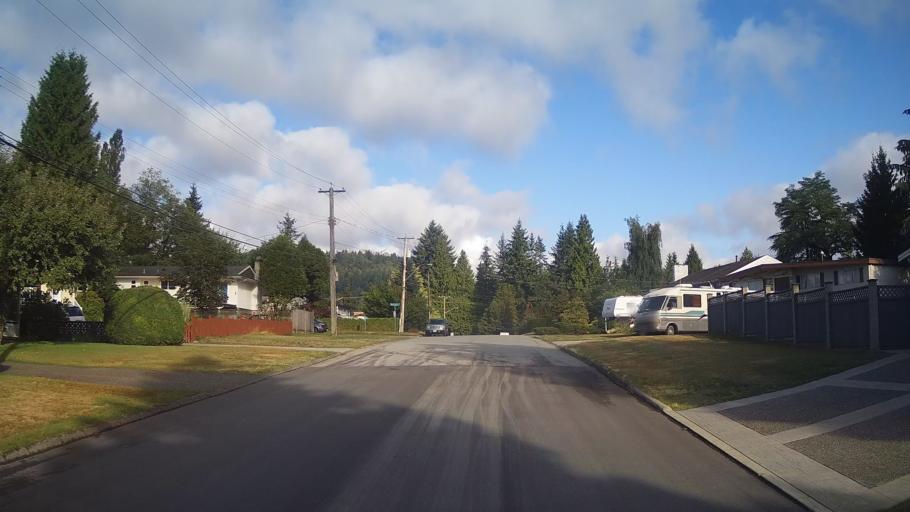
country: CA
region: British Columbia
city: Port Moody
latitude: 49.2743
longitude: -122.8781
